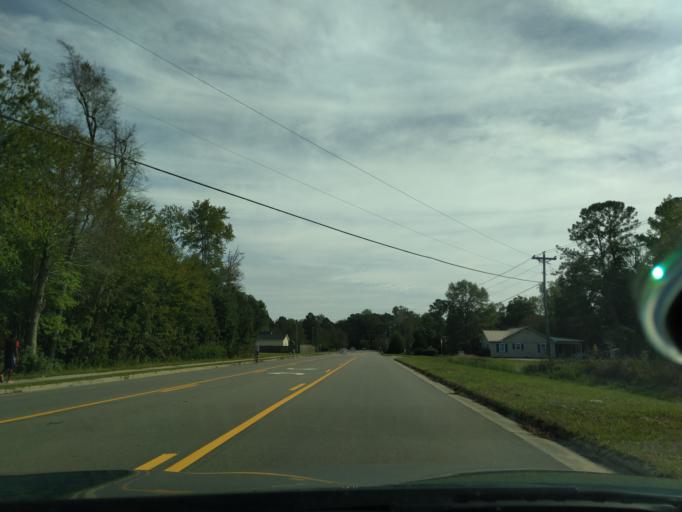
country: US
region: North Carolina
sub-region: Beaufort County
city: River Road
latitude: 35.5118
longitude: -77.0016
